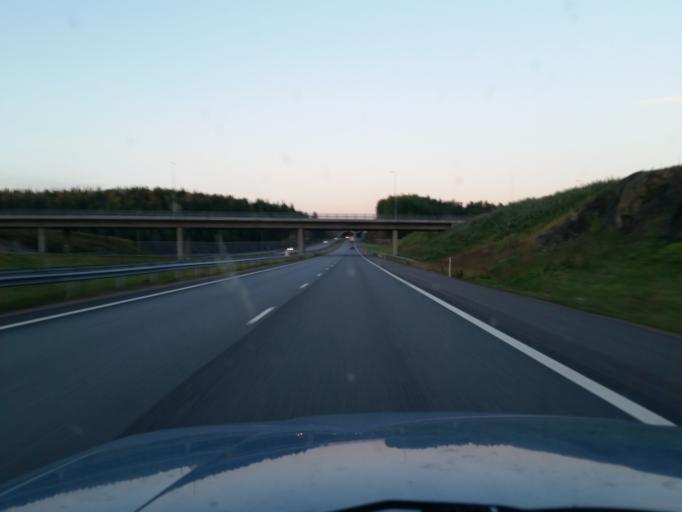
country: FI
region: Uusimaa
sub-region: Helsinki
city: Sammatti
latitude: 60.3784
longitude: 23.8029
